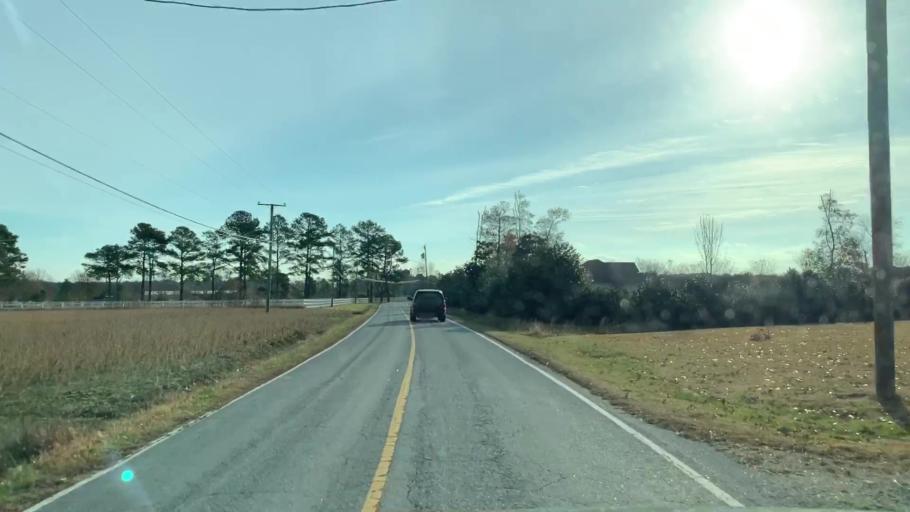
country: US
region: Virginia
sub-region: City of Virginia Beach
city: Virginia Beach
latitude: 36.6886
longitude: -76.0031
